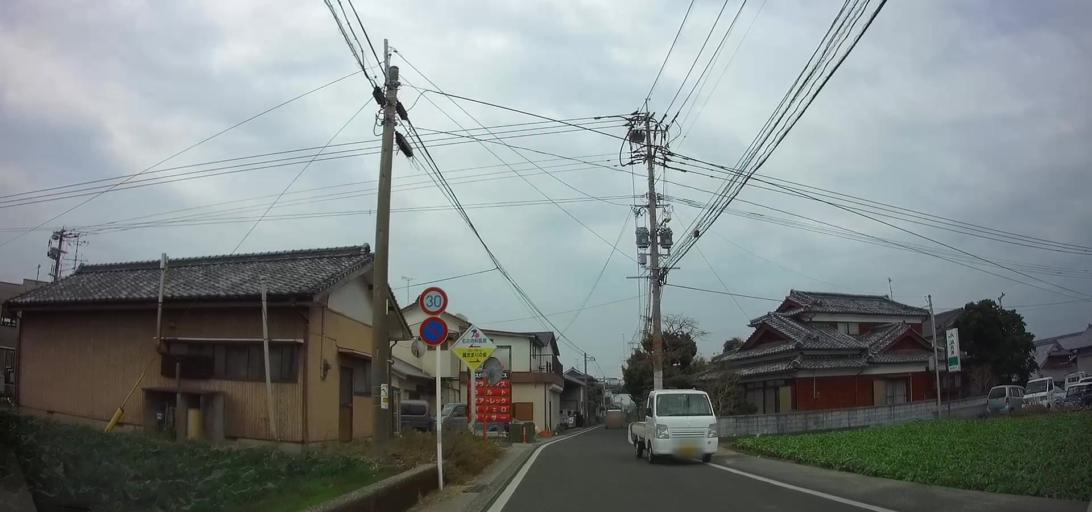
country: JP
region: Nagasaki
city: Shimabara
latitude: 32.6612
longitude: 130.2994
